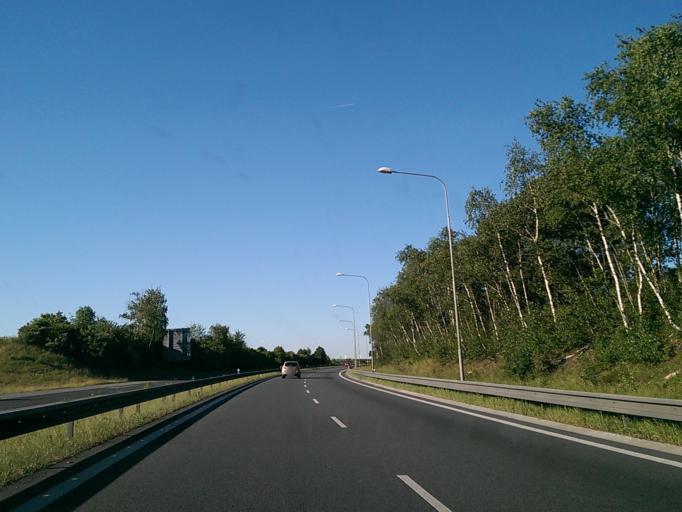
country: CZ
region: Praha
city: Cerny Most
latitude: 50.1163
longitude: 14.5889
